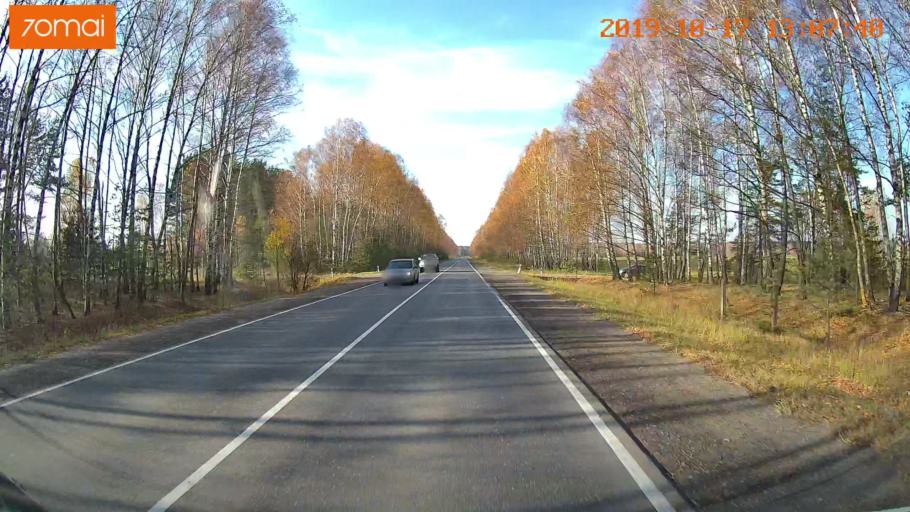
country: RU
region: Rjazan
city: Syntul
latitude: 54.9836
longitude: 41.2855
